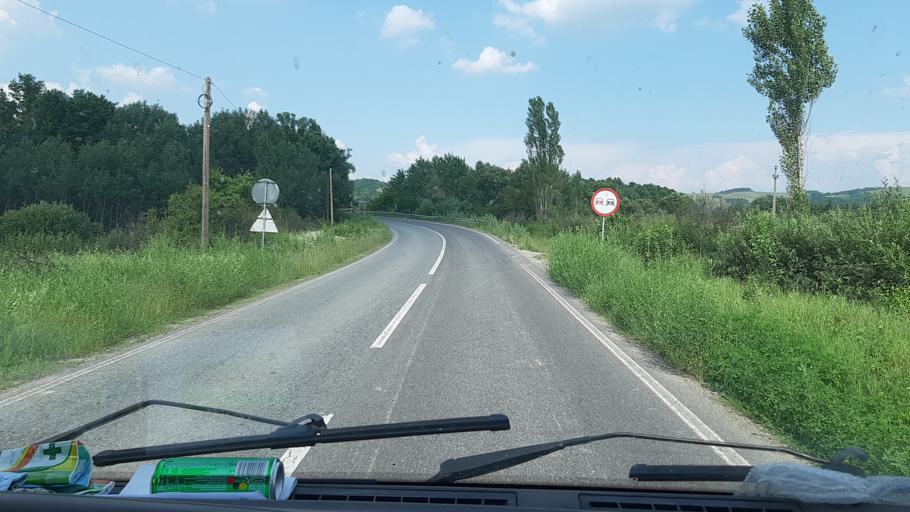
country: RO
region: Caras-Severin
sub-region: Comuna Farliug
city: Farliug
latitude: 45.5029
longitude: 21.8693
